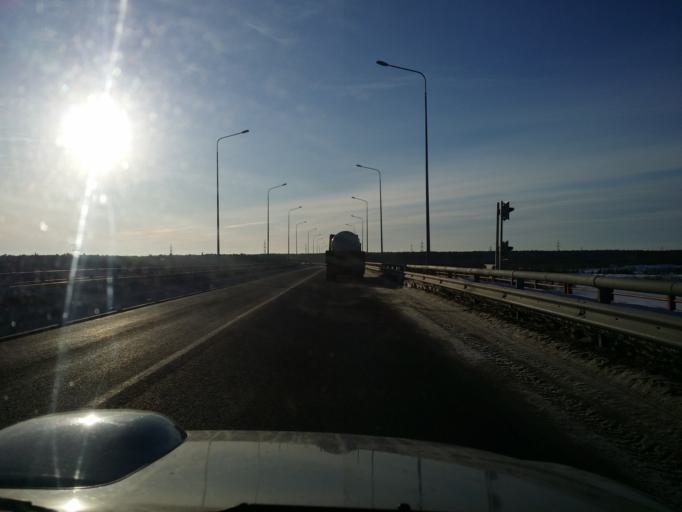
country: RU
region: Khanty-Mansiyskiy Avtonomnyy Okrug
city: Izluchinsk
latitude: 60.9355
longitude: 76.8880
